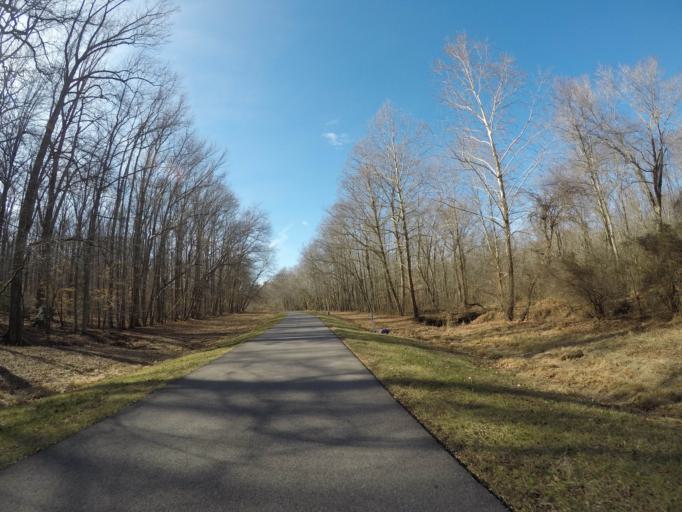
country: US
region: Maryland
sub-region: Charles County
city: Bennsville
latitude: 38.5972
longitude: -77.0076
